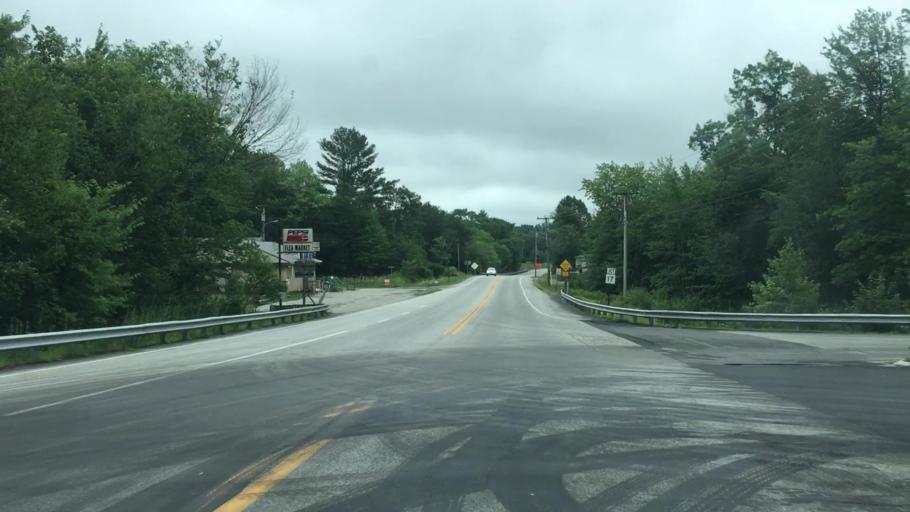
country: US
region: Maine
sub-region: Kennebec County
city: Chelsea
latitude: 44.2782
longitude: -69.6845
